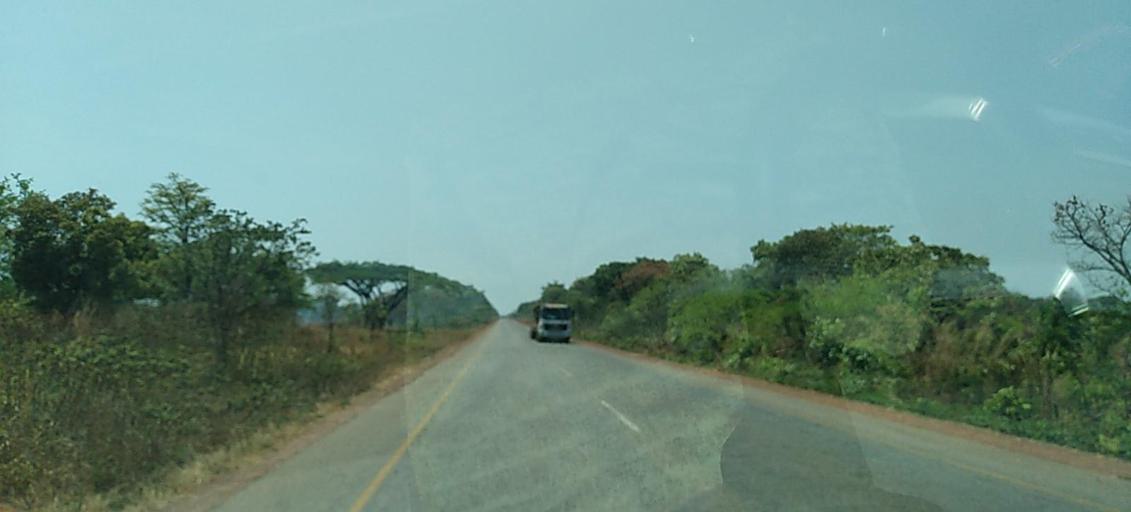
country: ZM
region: North-Western
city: Solwezi
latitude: -12.3825
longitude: 26.1948
